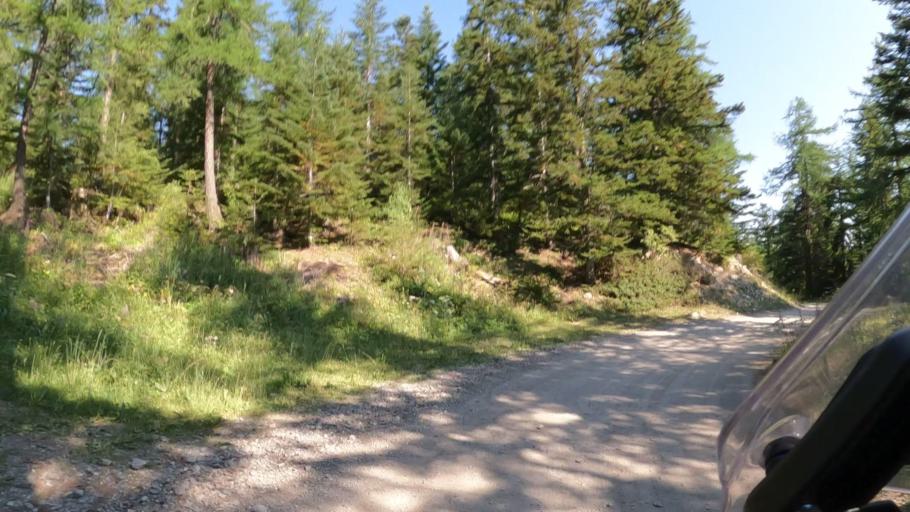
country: FR
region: Provence-Alpes-Cote d'Azur
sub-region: Departement des Hautes-Alpes
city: Embrun
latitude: 44.5916
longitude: 6.5738
